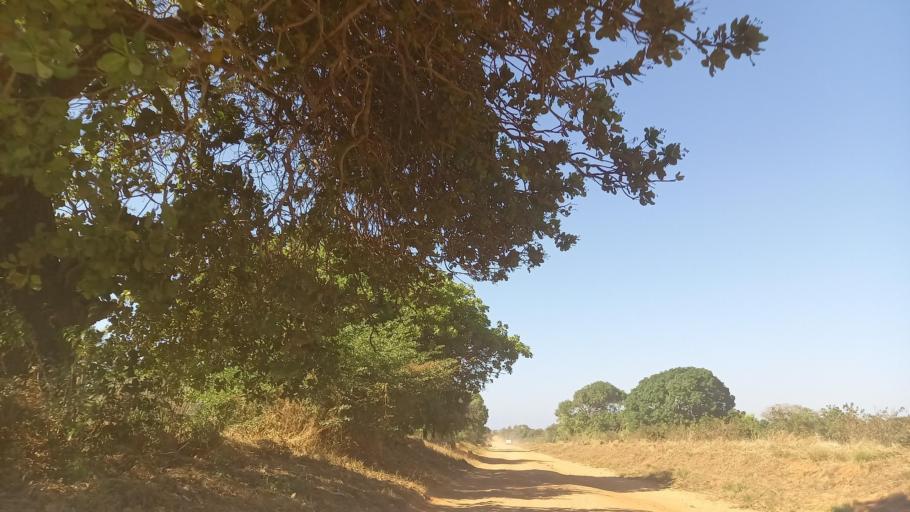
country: MZ
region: Cabo Delgado
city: Pemba
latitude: -13.1527
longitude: 40.5576
